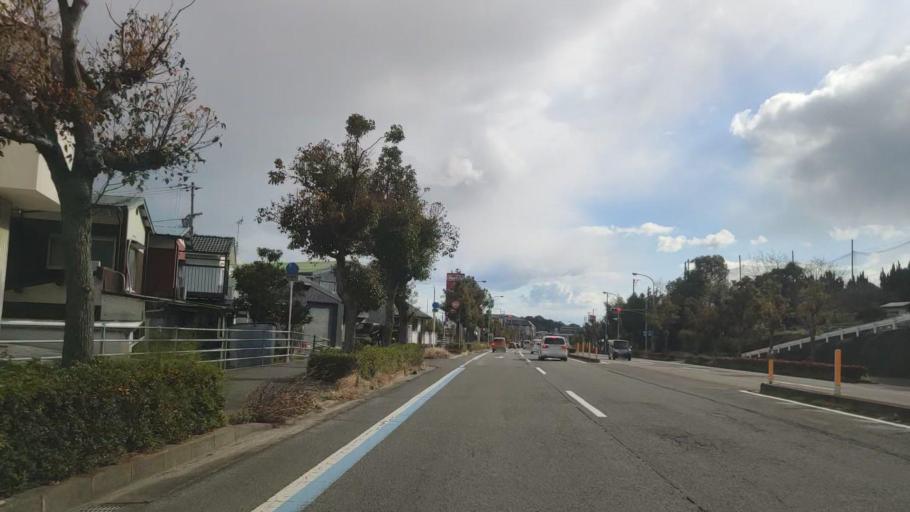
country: JP
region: Ehime
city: Hojo
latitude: 34.0613
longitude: 132.9632
